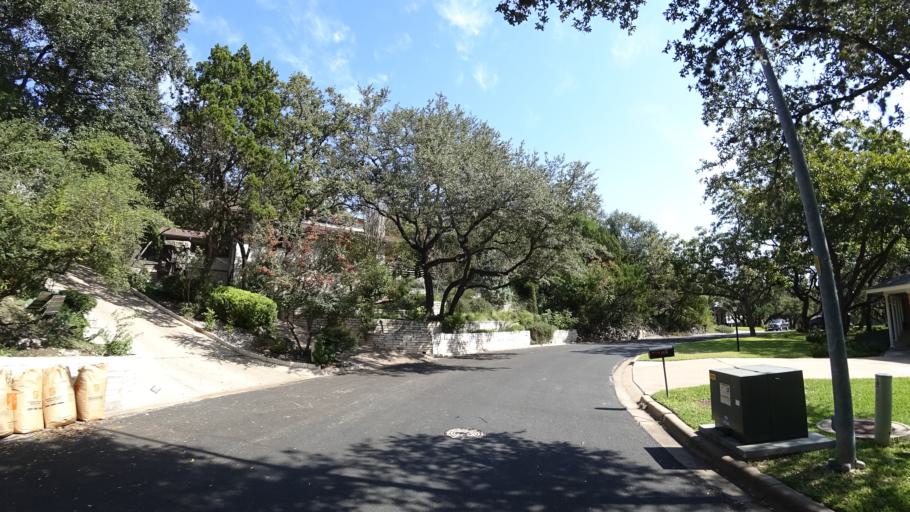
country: US
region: Texas
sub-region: Travis County
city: West Lake Hills
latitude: 30.3476
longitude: -97.7600
